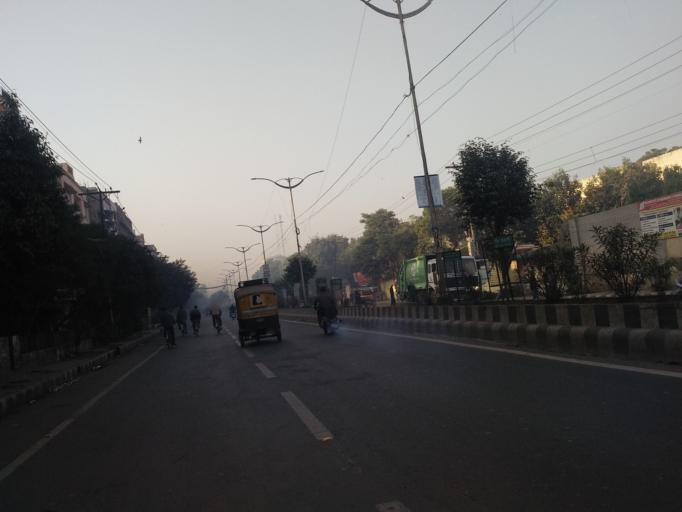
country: IN
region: Punjab
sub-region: Amritsar
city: Amritsar
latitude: 31.6224
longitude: 74.8670
